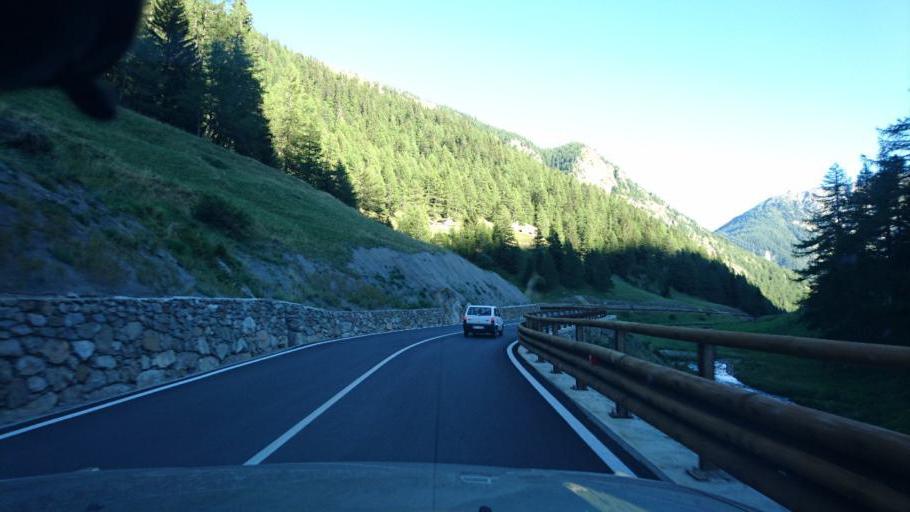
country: IT
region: Aosta Valley
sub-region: Valle d'Aosta
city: San Leonardo
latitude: 45.8437
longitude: 7.1779
